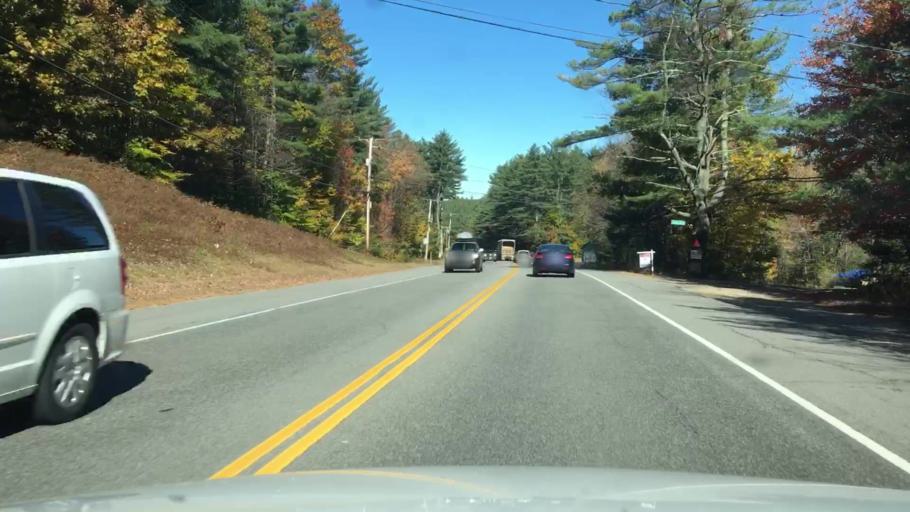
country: US
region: New Hampshire
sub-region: Carroll County
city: Ossipee
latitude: 43.7166
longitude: -71.1235
